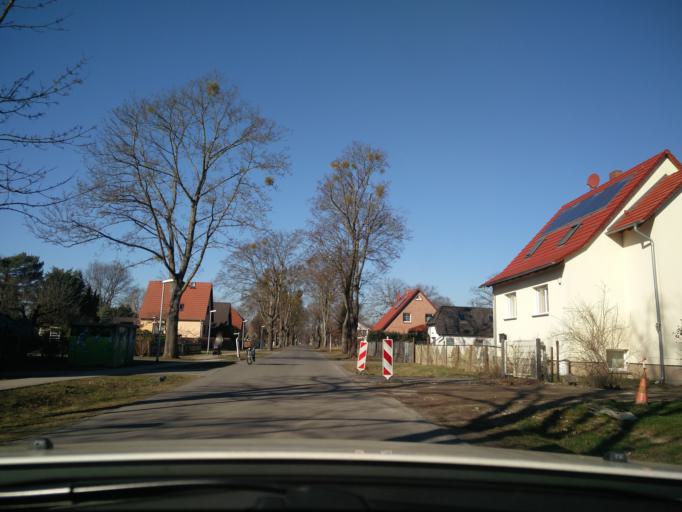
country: DE
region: Brandenburg
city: Brieselang
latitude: 52.5812
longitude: 12.9901
